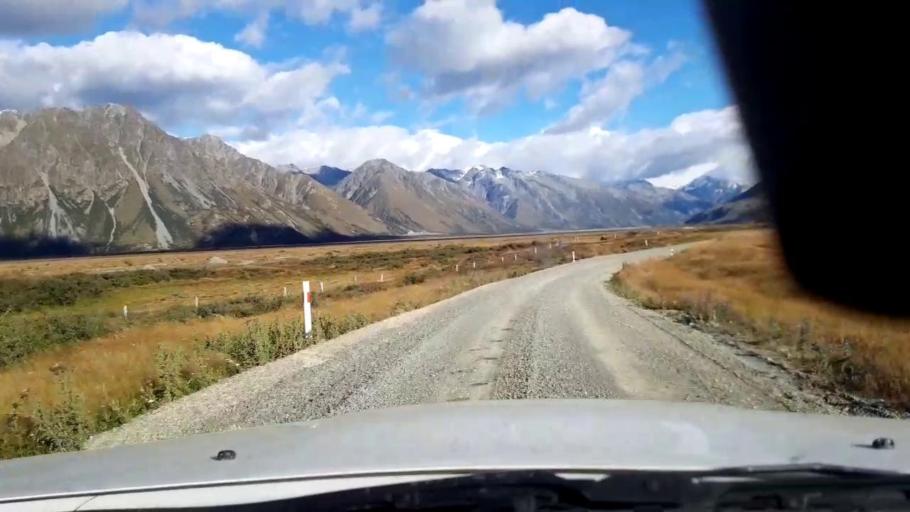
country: NZ
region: Canterbury
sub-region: Timaru District
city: Pleasant Point
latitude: -43.7404
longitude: 170.5695
